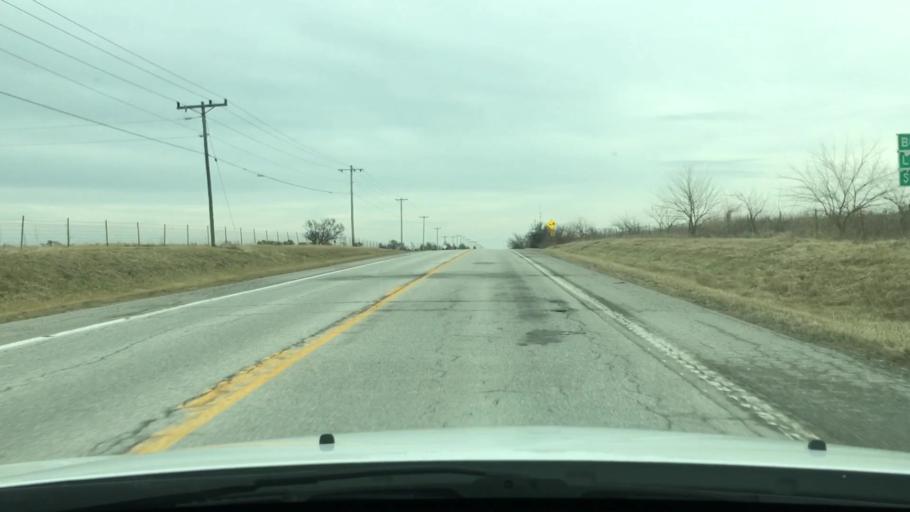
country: US
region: Missouri
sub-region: Pike County
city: Bowling Green
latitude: 39.3452
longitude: -91.3333
